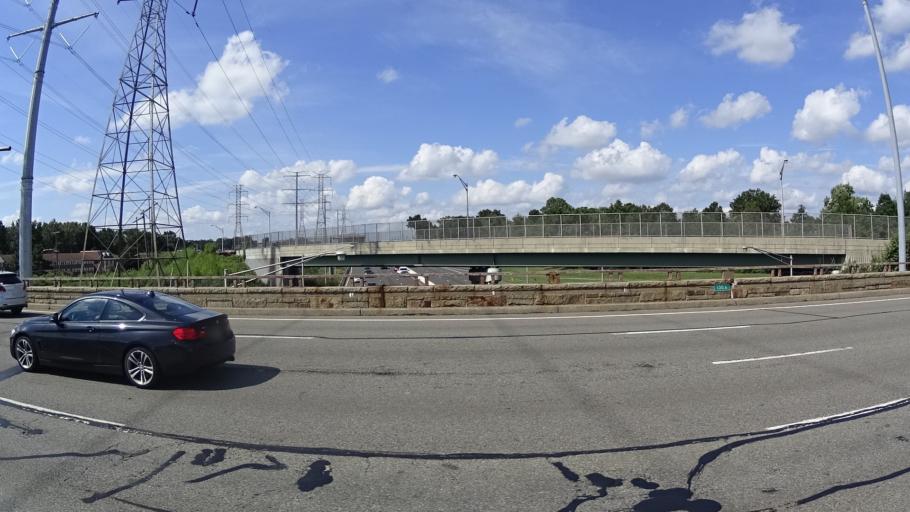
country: US
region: New Jersey
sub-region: Middlesex County
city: Iselin
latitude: 40.5527
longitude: -74.3175
